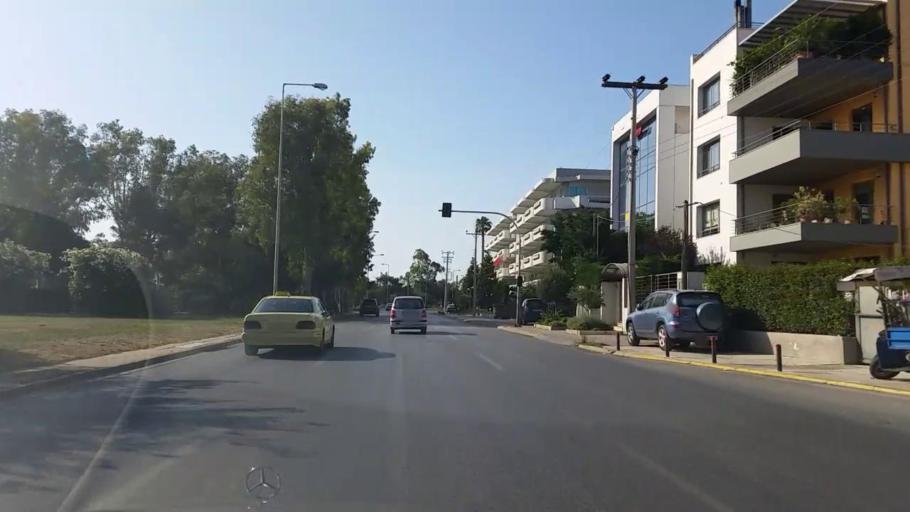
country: GR
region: Attica
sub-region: Nomarchia Athinas
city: Glyfada
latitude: 37.8522
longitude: 23.7527
